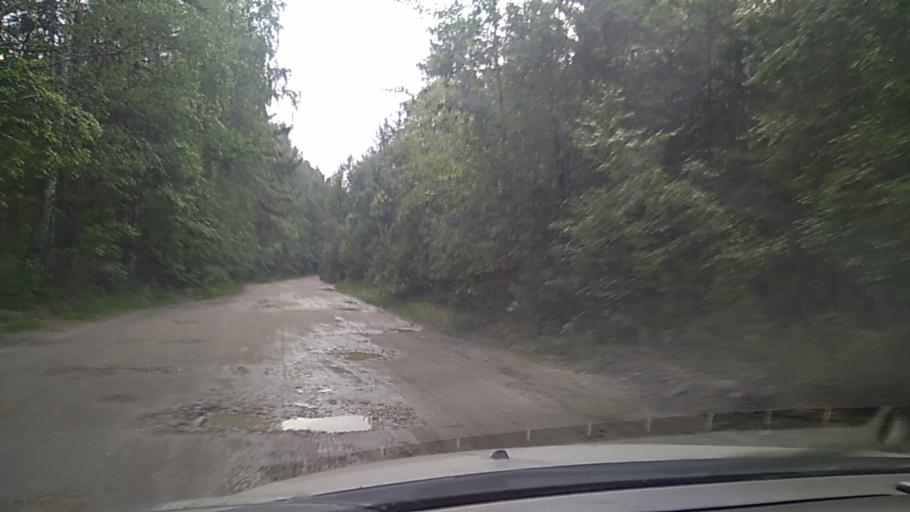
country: RU
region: Chelyabinsk
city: Kyshtym
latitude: 55.6777
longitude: 60.5870
